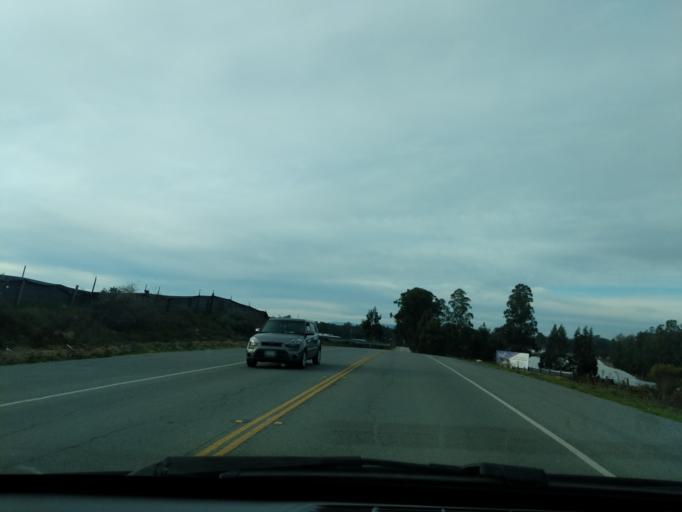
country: US
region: California
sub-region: San Luis Obispo County
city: Callender
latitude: 35.0354
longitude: -120.5624
